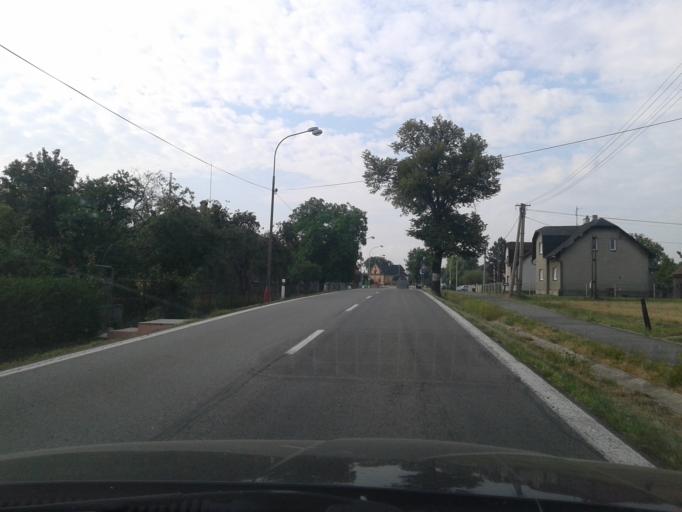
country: CZ
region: Moravskoslezsky
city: Orlova
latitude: 49.8633
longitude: 18.4443
